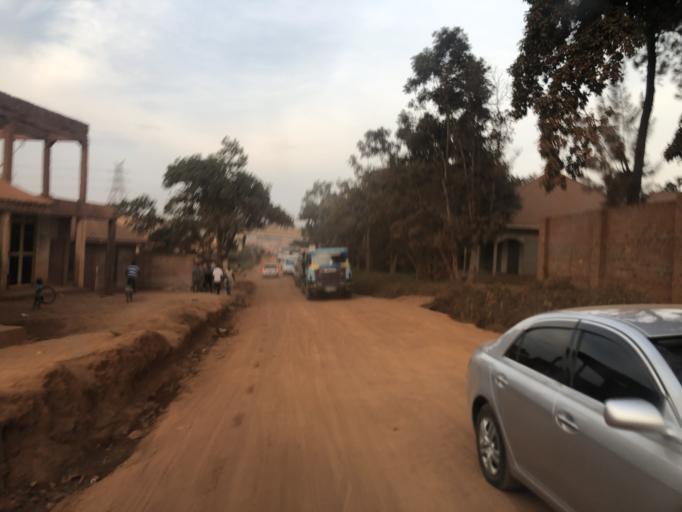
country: UG
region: Central Region
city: Kampala Central Division
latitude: 0.3001
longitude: 32.5108
